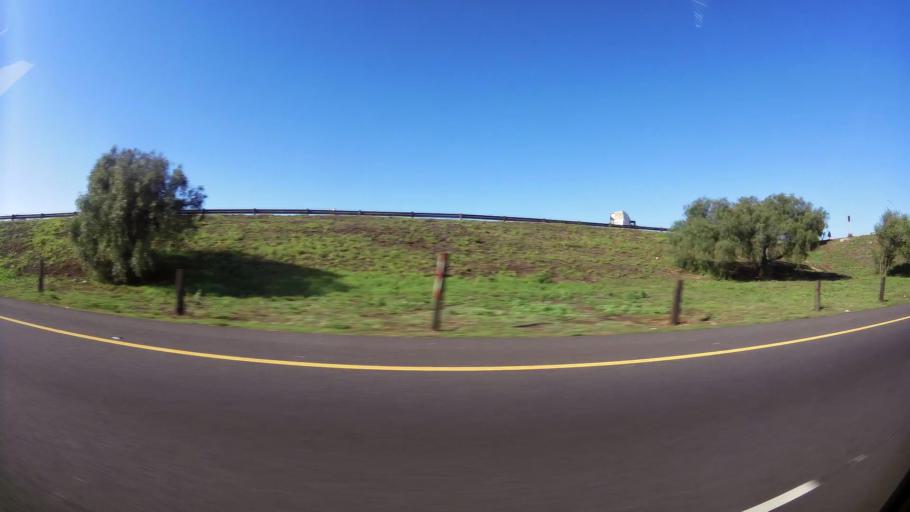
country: ZA
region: Eastern Cape
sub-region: Nelson Mandela Bay Metropolitan Municipality
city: Port Elizabeth
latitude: -33.9230
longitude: 25.5674
